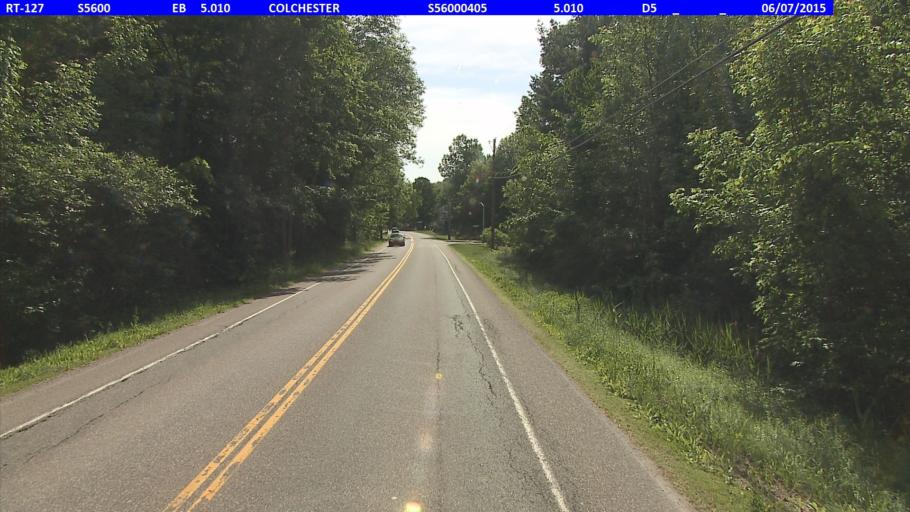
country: US
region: Vermont
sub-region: Chittenden County
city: Winooski
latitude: 44.5295
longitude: -73.1885
